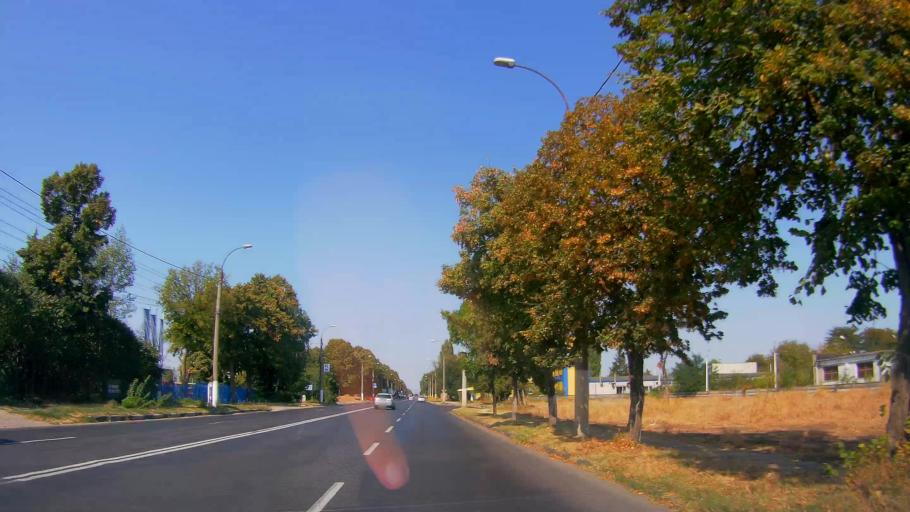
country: RO
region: Giurgiu
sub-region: Comuna Fratesti
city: Remus
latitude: 43.9211
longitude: 25.9734
